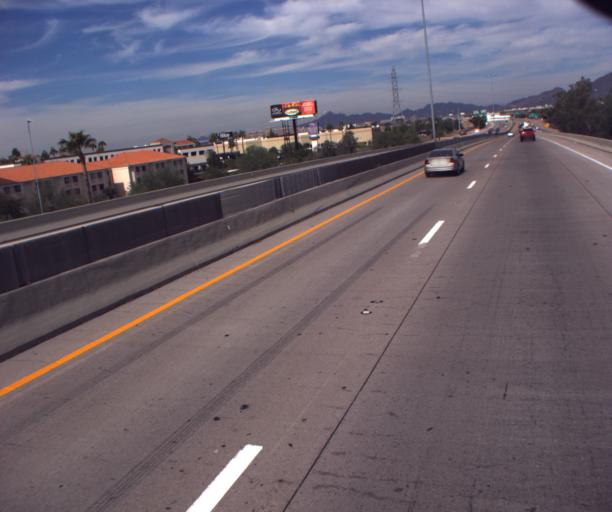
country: US
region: Arizona
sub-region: Maricopa County
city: Tempe Junction
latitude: 33.4229
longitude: -111.9780
